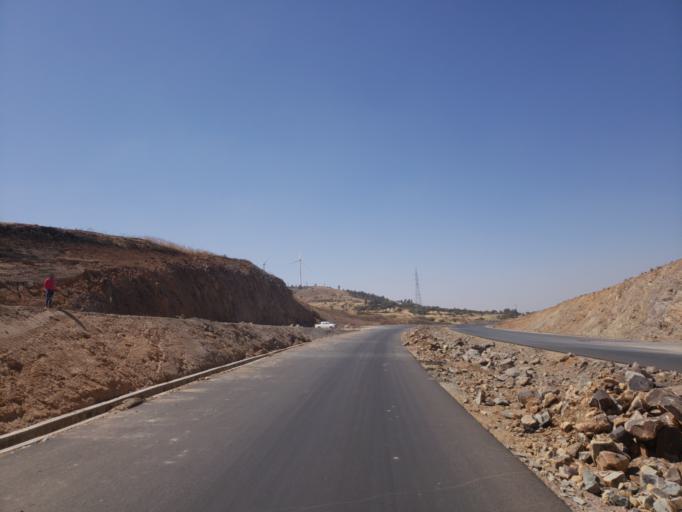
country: ET
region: Oromiya
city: Mojo
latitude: 8.5662
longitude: 39.1630
